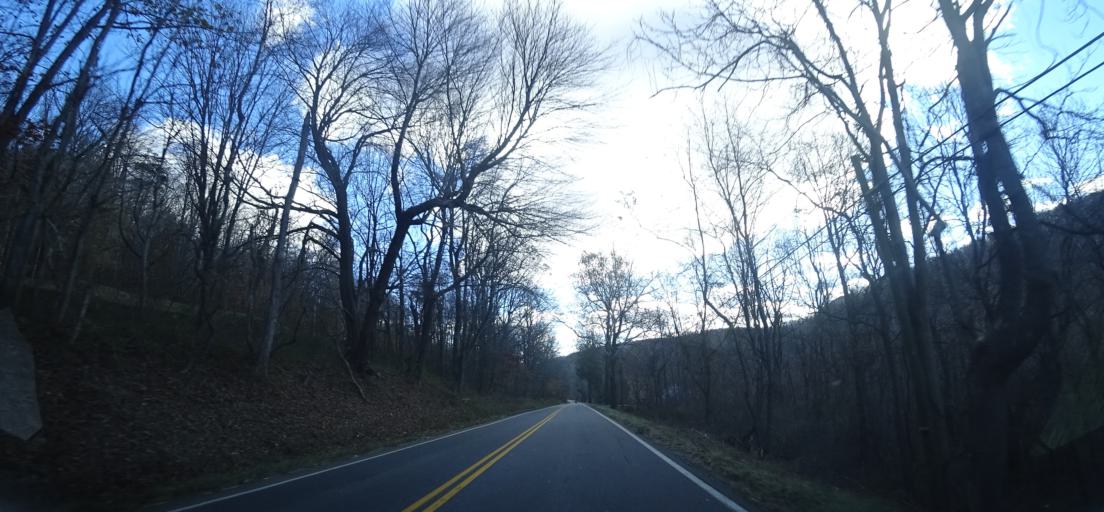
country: US
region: Virginia
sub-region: Greene County
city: Stanardsville
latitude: 38.3352
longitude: -78.5018
